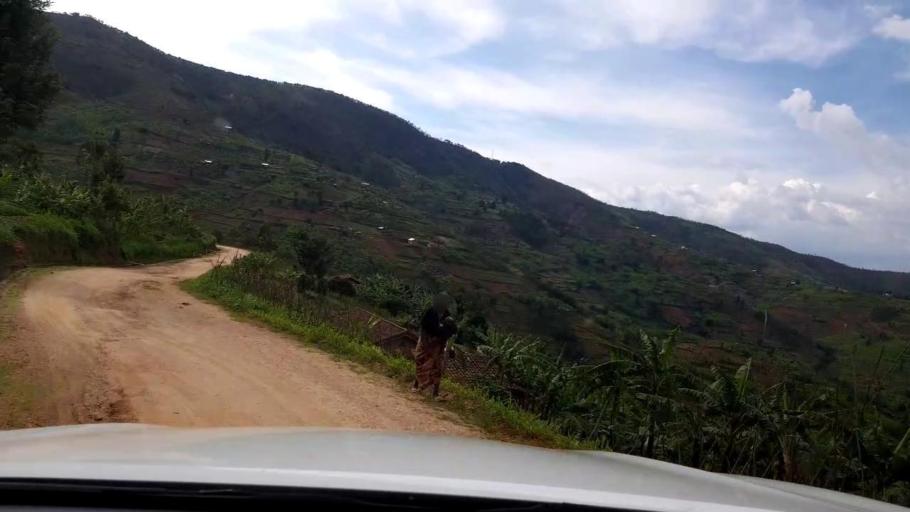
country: RW
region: Southern Province
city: Gitarama
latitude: -1.9783
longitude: 29.7109
